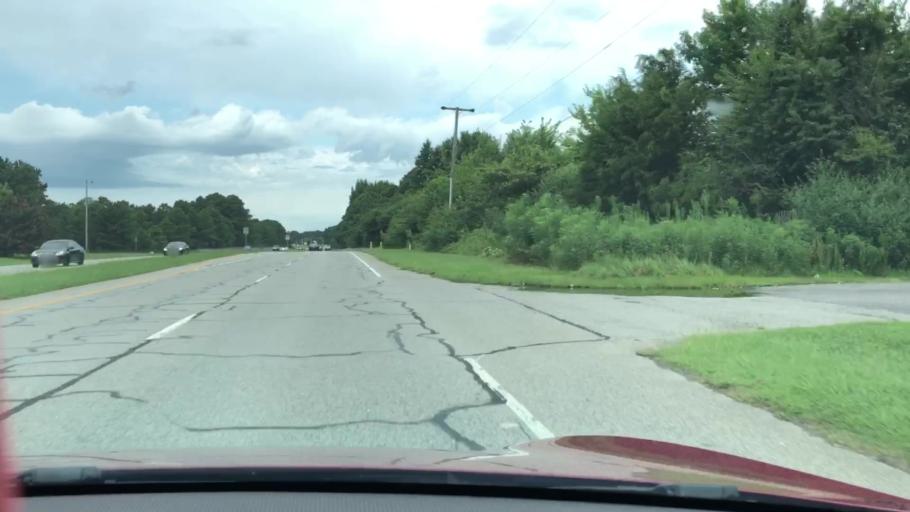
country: US
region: Virginia
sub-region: City of Virginia Beach
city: Virginia Beach
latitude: 36.8271
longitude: -76.0100
